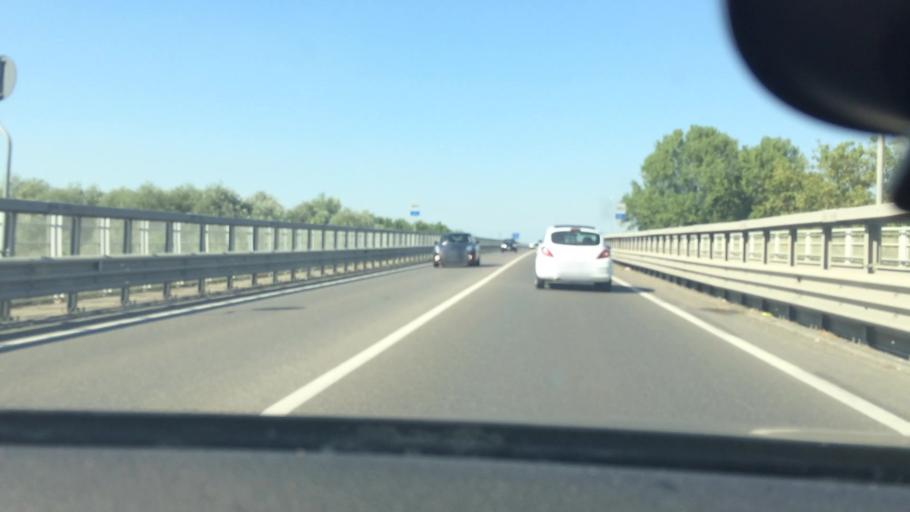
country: IT
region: Emilia-Romagna
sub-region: Provincia di Piacenza
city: Piacenza
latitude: 45.0619
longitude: 9.7041
